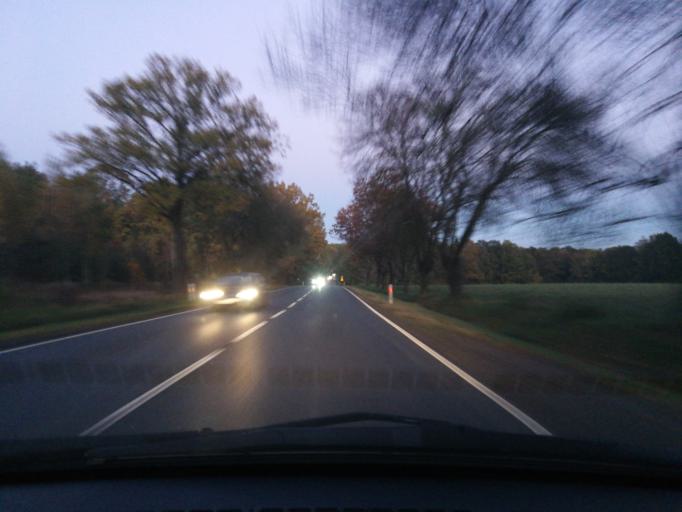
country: PL
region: Lodz Voivodeship
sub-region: Powiat brzezinski
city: Rogow
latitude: 51.8059
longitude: 19.8365
